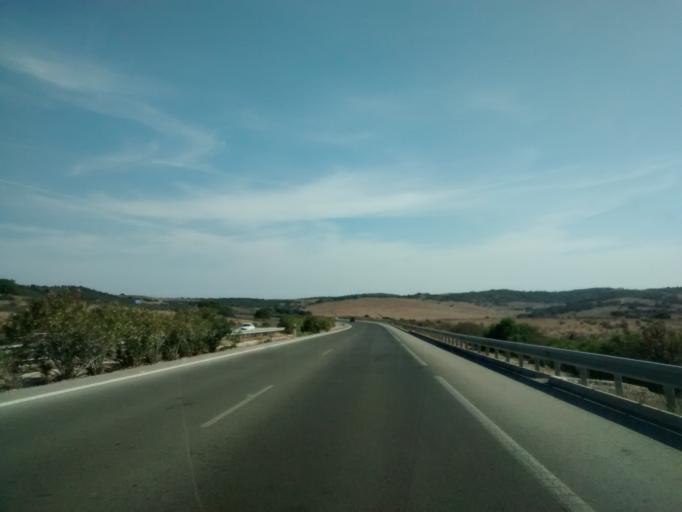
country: ES
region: Andalusia
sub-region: Provincia de Cadiz
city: Conil de la Frontera
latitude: 36.3320
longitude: -6.0513
